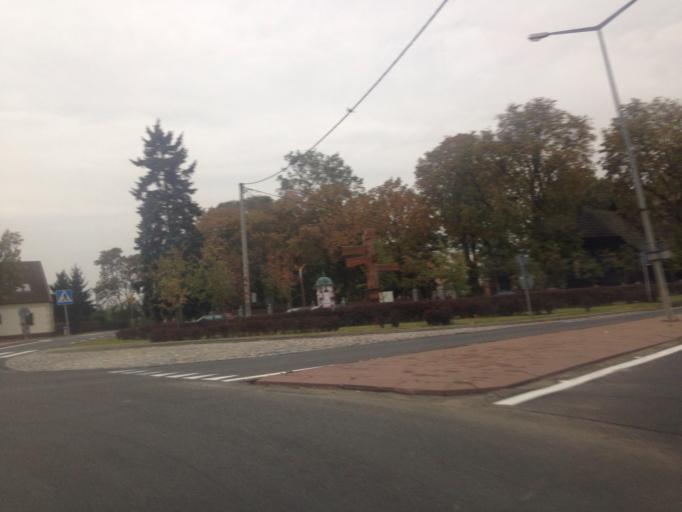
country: PL
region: Greater Poland Voivodeship
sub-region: Powiat gnieznienski
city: Lubowo
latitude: 52.5117
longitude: 17.4529
